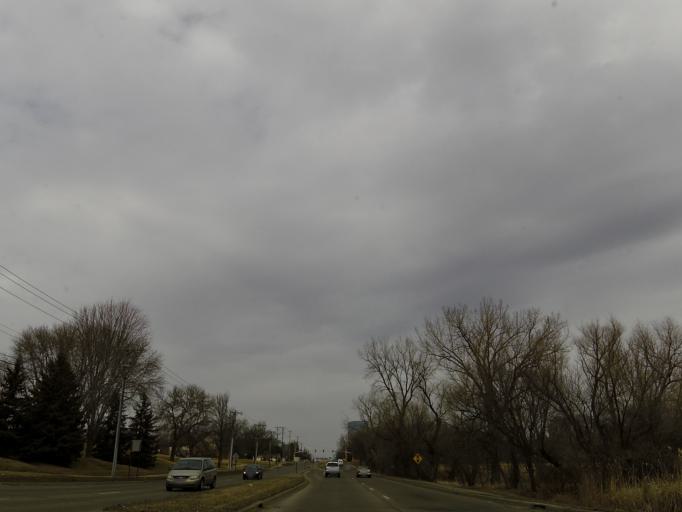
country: US
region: Minnesota
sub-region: Hennepin County
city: Bloomington
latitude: 44.8491
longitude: -93.3292
